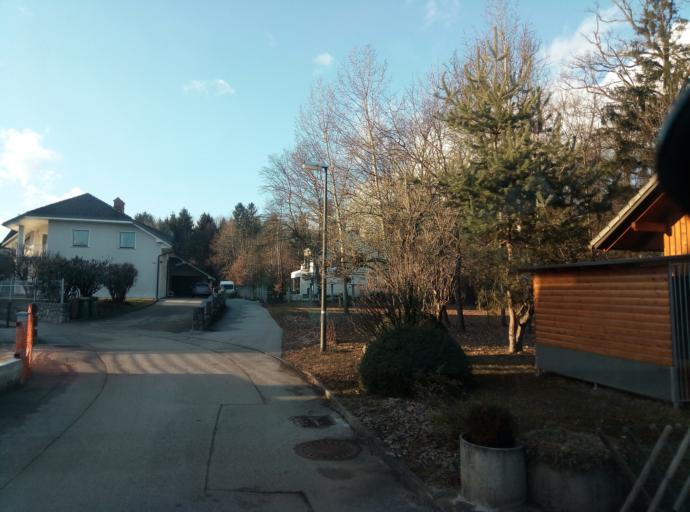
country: SI
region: Sencur
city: Hrastje
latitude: 46.2227
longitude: 14.3826
